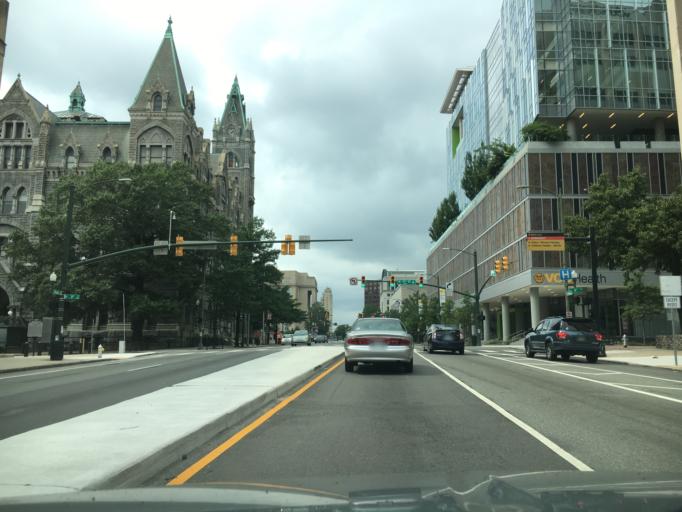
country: US
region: Virginia
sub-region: City of Richmond
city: Richmond
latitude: 37.5395
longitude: -77.4316
